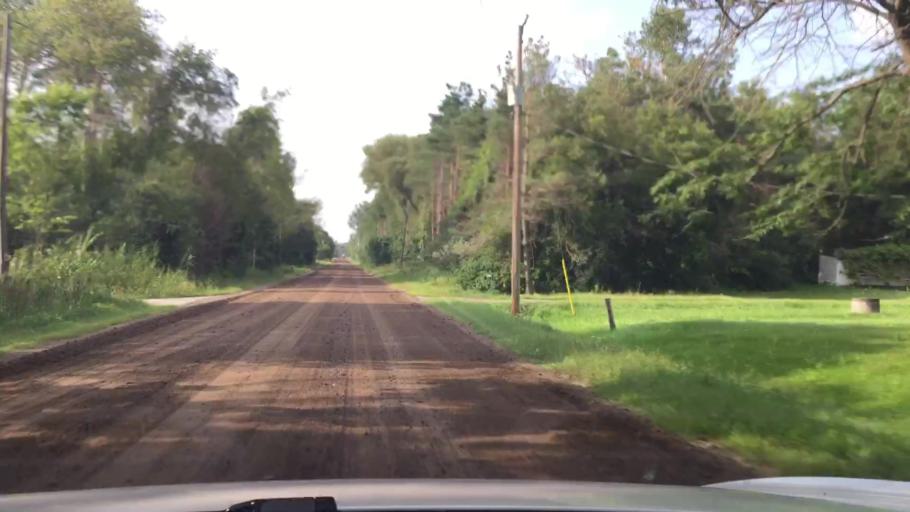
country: CA
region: Ontario
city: Oshawa
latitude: 43.9309
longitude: -78.7432
